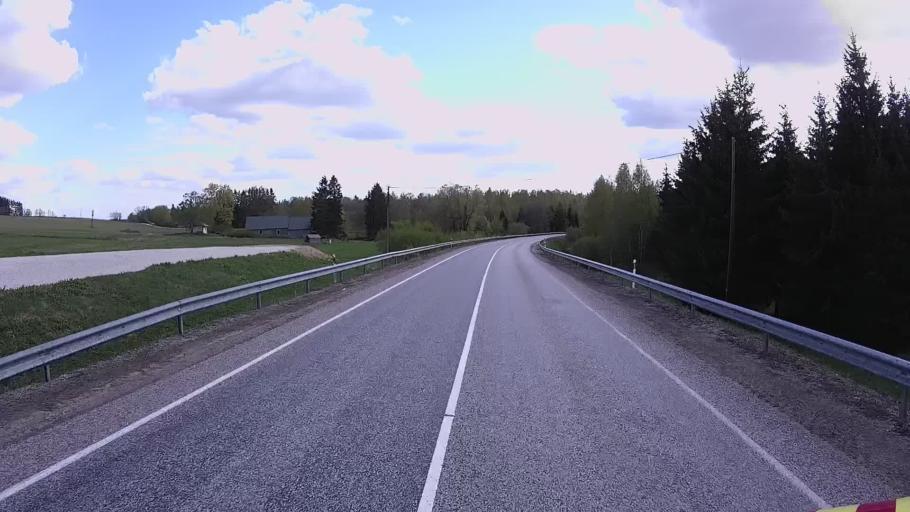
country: EE
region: Jogevamaa
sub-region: Jogeva linn
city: Jogeva
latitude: 58.7774
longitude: 26.4725
